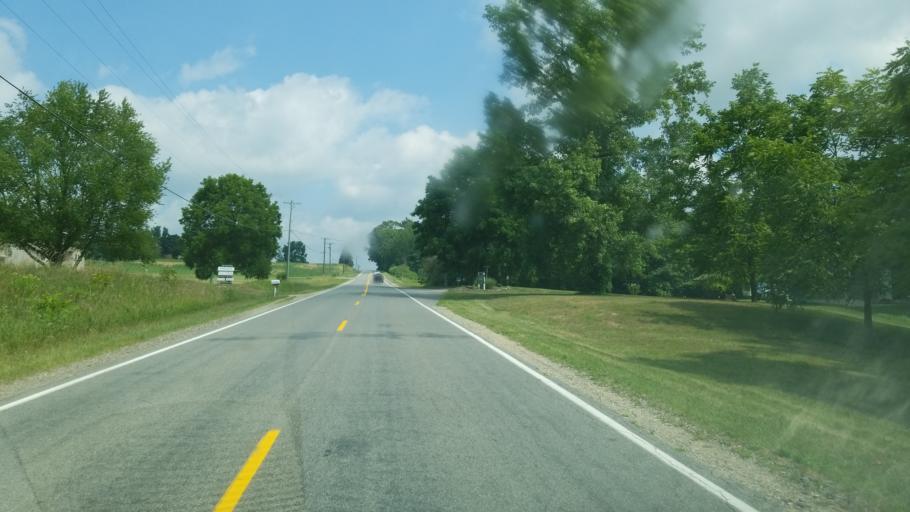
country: US
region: Michigan
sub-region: Kent County
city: Kent City
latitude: 43.2107
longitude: -85.7114
